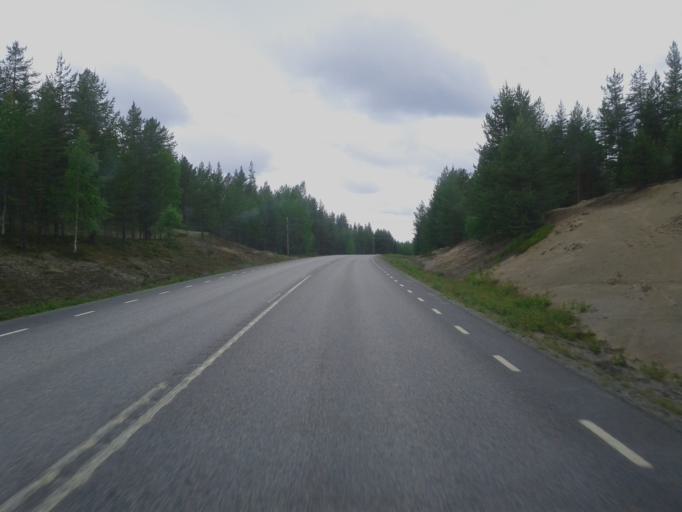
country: SE
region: Vaesterbotten
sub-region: Skelleftea Kommun
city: Langsele
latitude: 64.9253
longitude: 20.0246
